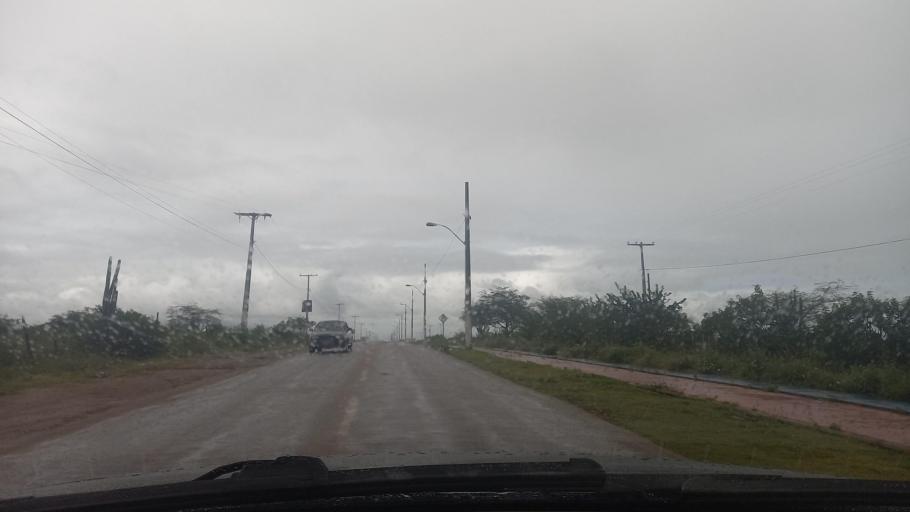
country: BR
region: Bahia
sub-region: Paulo Afonso
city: Paulo Afonso
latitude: -9.3598
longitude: -38.2737
